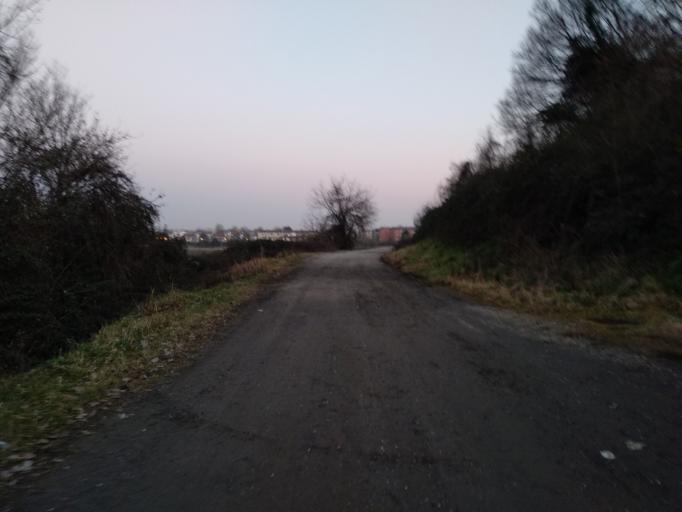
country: IT
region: Veneto
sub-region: Provincia di Padova
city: Battaglia Terme
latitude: 45.2950
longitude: 11.7757
